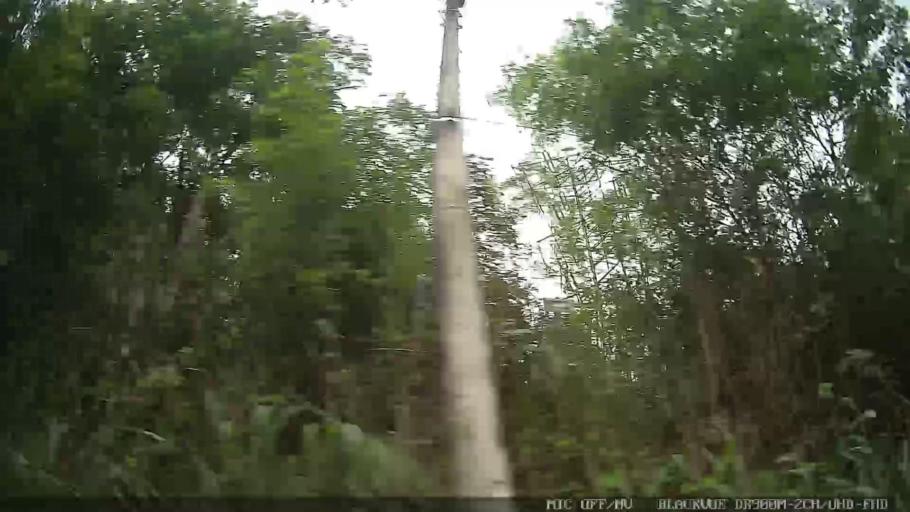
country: BR
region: Sao Paulo
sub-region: Osasco
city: Osasco
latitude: -23.4644
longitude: -46.7388
